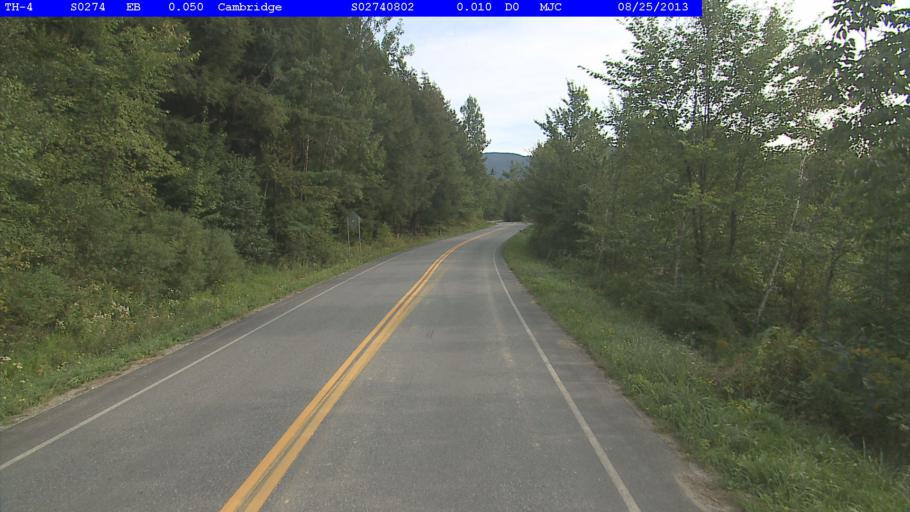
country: US
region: Vermont
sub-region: Lamoille County
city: Johnson
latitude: 44.6824
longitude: -72.7711
